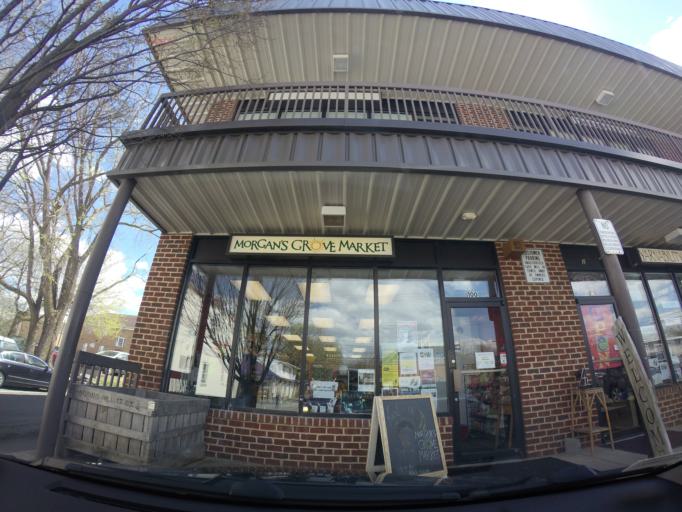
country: US
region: West Virginia
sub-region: Jefferson County
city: Shepherdstown
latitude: 39.4289
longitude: -77.8048
